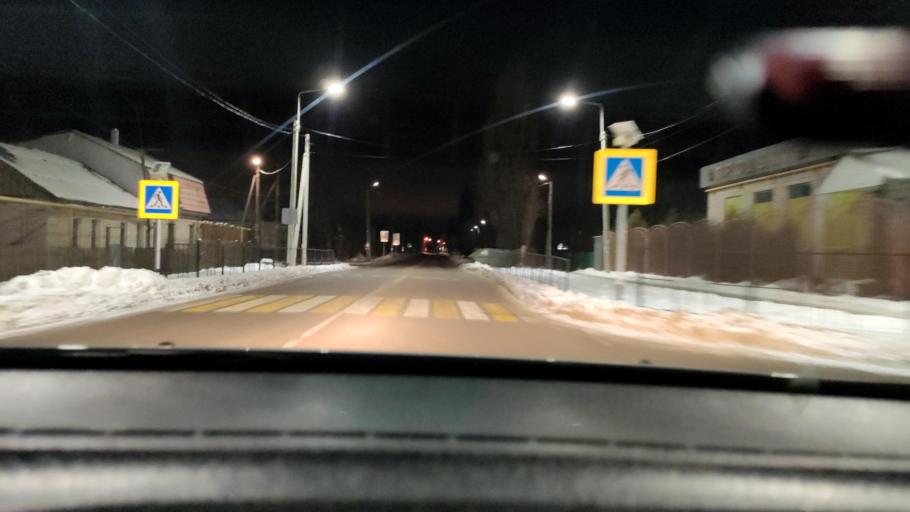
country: RU
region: Voronezj
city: Ramon'
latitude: 51.9196
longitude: 39.3446
